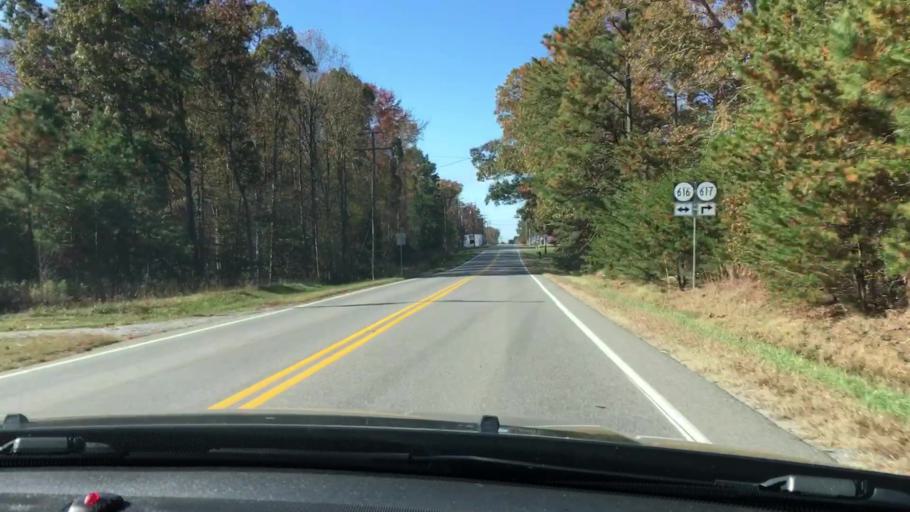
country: US
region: Virginia
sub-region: King William County
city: King William
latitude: 37.7164
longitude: -77.0700
